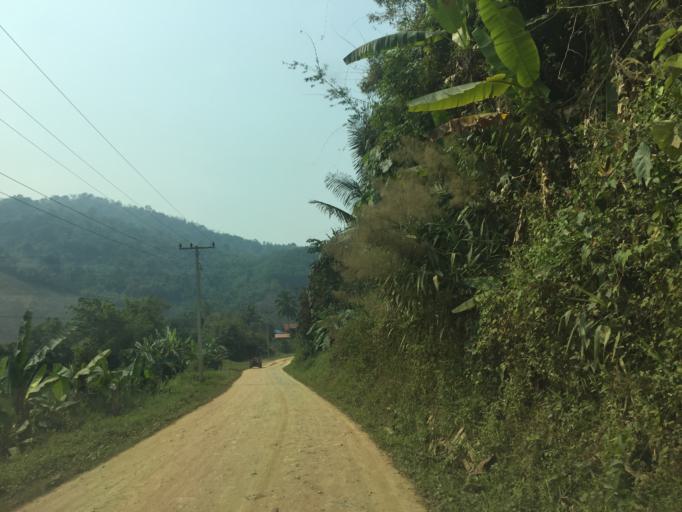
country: TH
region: Phayao
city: Phu Sang
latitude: 19.6089
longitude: 100.5393
